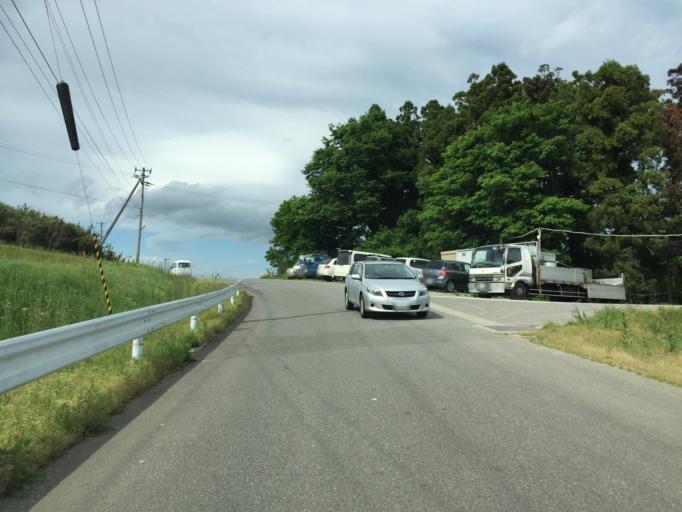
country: JP
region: Fukushima
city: Nihommatsu
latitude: 37.6415
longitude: 140.5253
